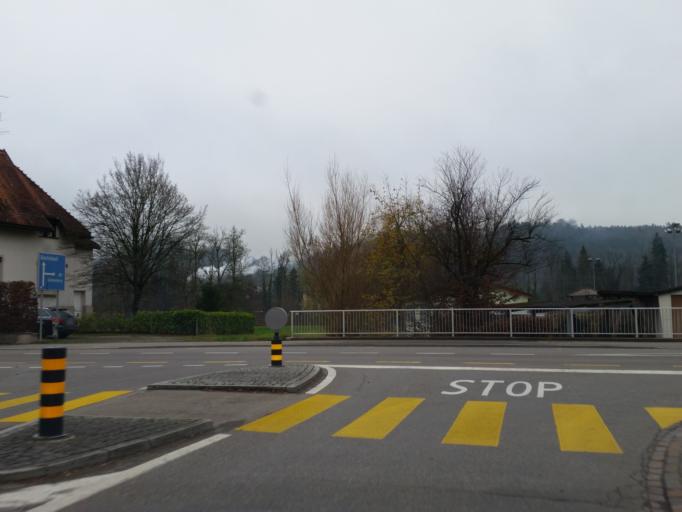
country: CH
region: Thurgau
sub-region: Weinfelden District
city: Sulgen
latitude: 47.5259
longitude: 9.1993
